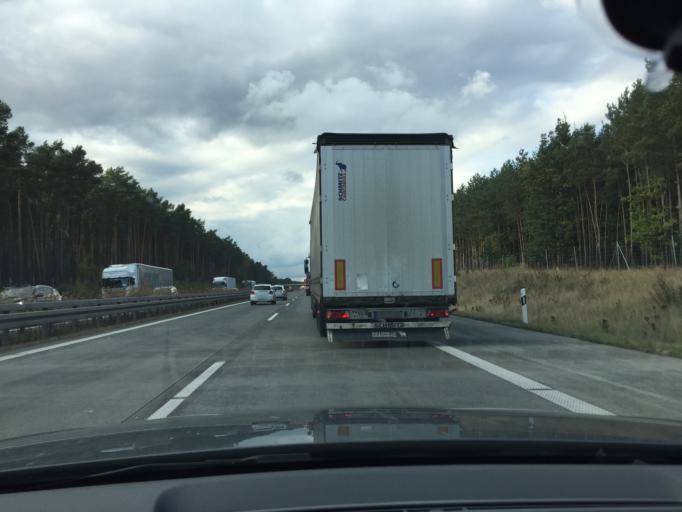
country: DE
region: Brandenburg
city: Luebben
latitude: 51.8817
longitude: 13.8725
